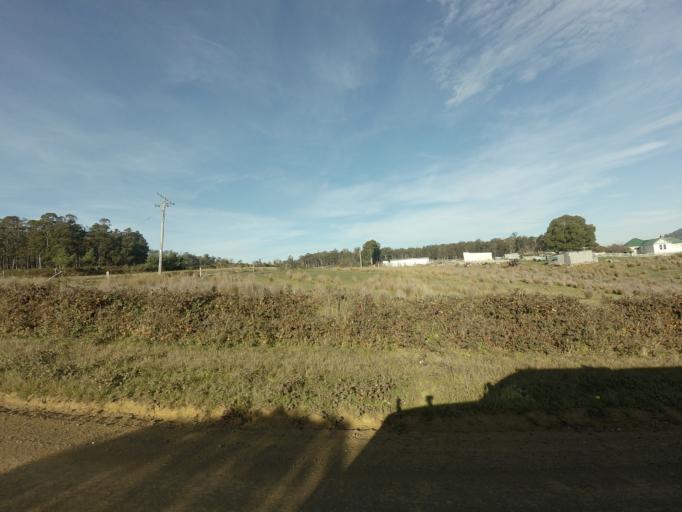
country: AU
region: Tasmania
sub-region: Brighton
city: Bridgewater
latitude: -42.4616
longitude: 147.3778
